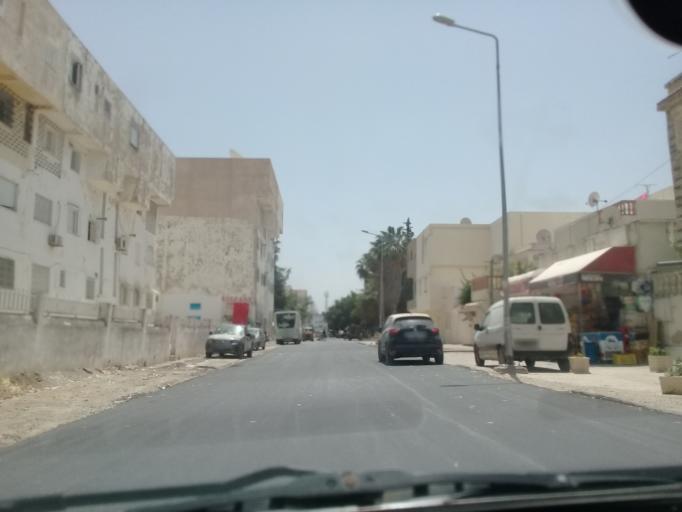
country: TN
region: Ariana
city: Ariana
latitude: 36.8320
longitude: 10.1992
